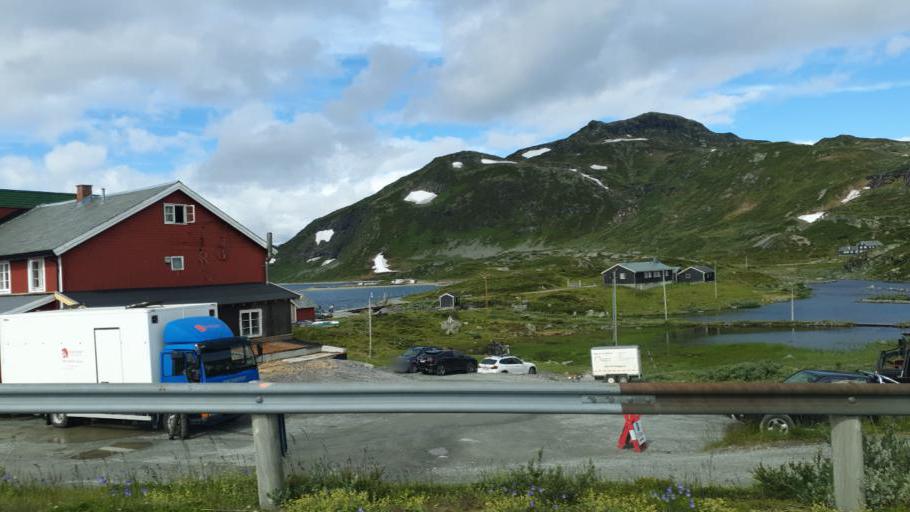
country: NO
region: Oppland
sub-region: Vestre Slidre
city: Slidre
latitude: 61.3280
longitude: 8.7999
